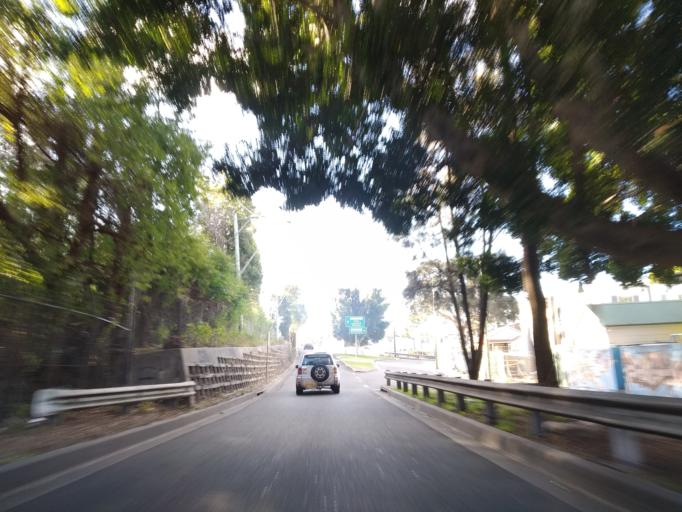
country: AU
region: New South Wales
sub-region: Ashfield
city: Summer Hill
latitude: -33.8911
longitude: 151.1452
